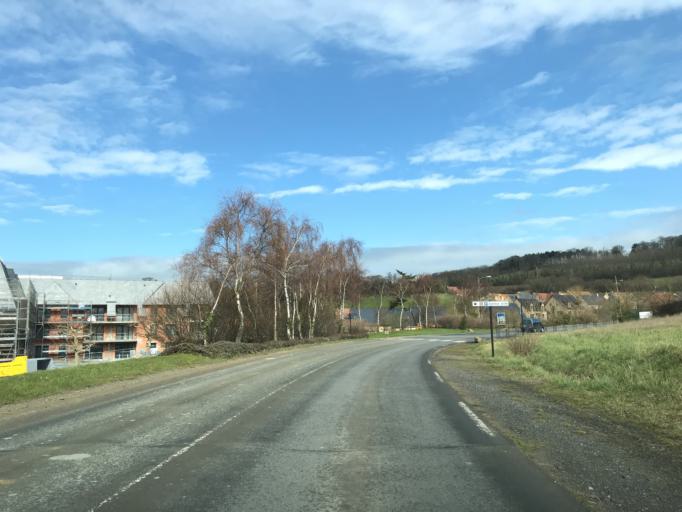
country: FR
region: Lower Normandy
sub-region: Departement du Calvados
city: Dives-sur-Mer
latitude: 49.2849
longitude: -0.0937
